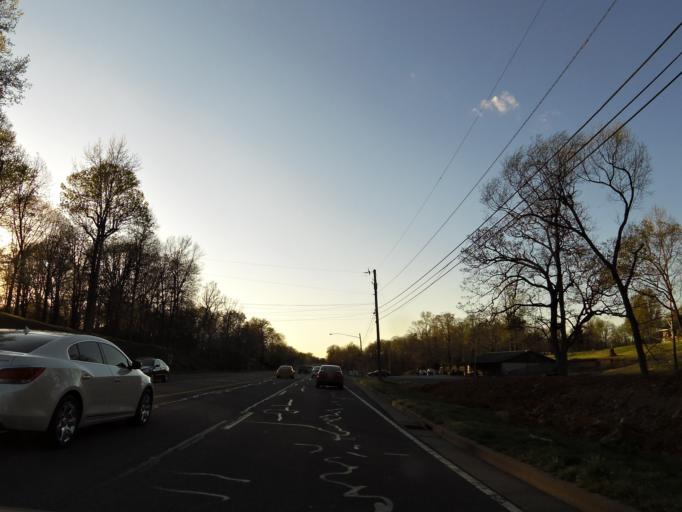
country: US
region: Tennessee
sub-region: Robertson County
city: Ridgetop
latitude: 36.4001
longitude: -86.7747
